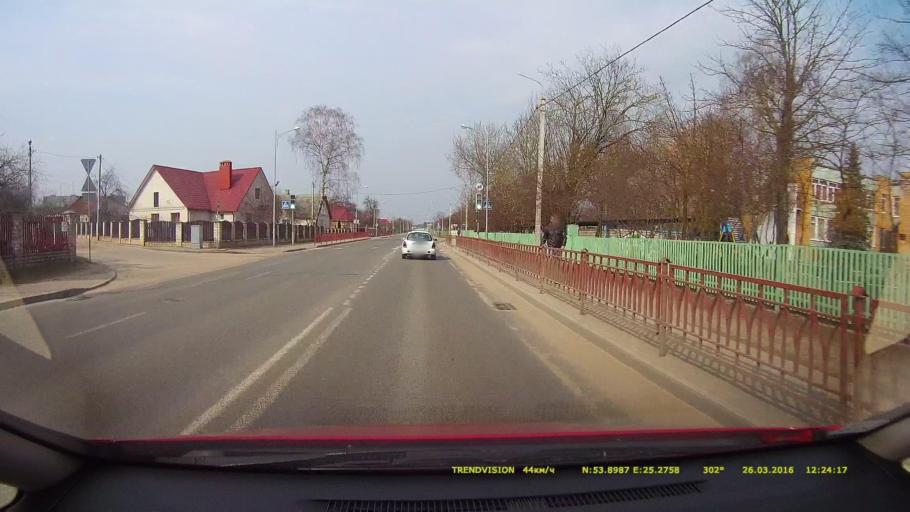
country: BY
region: Grodnenskaya
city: Lida
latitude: 53.8988
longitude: 25.2754
